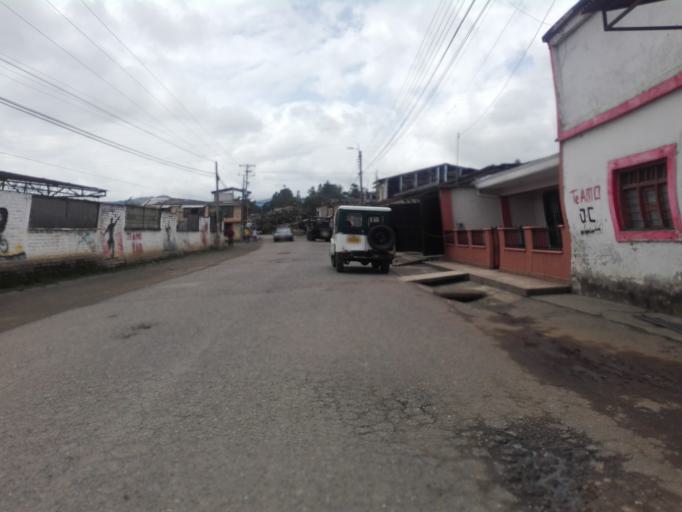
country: CO
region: Cauca
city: Popayan
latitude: 2.3512
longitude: -76.6775
